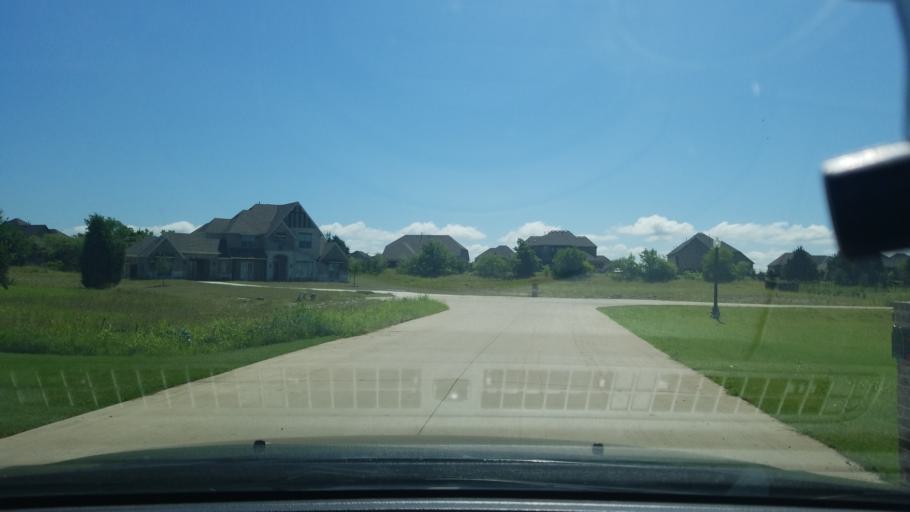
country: US
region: Texas
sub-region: Dallas County
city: Sunnyvale
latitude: 32.8025
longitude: -96.5710
